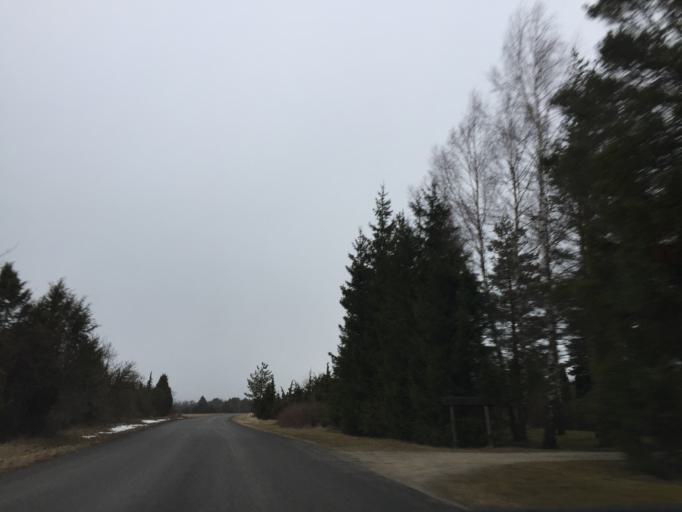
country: EE
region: Laeaene
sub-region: Lihula vald
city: Lihula
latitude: 58.6396
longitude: 23.6326
